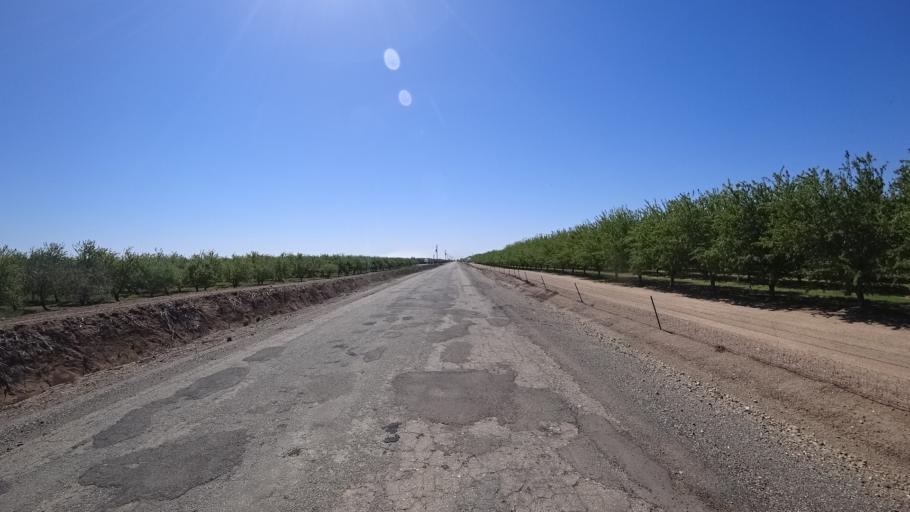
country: US
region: California
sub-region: Glenn County
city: Orland
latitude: 39.6487
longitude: -122.2346
